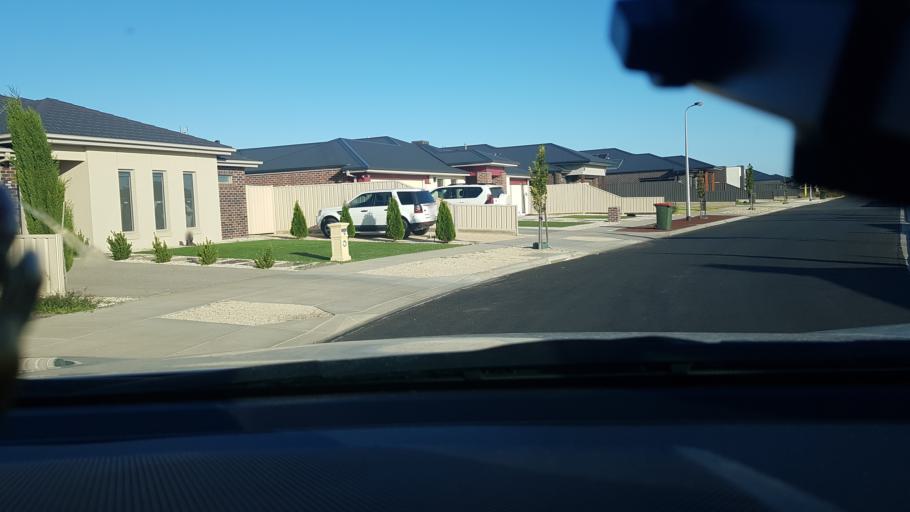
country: AU
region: Victoria
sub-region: Horsham
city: Horsham
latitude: -36.7147
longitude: 142.1759
